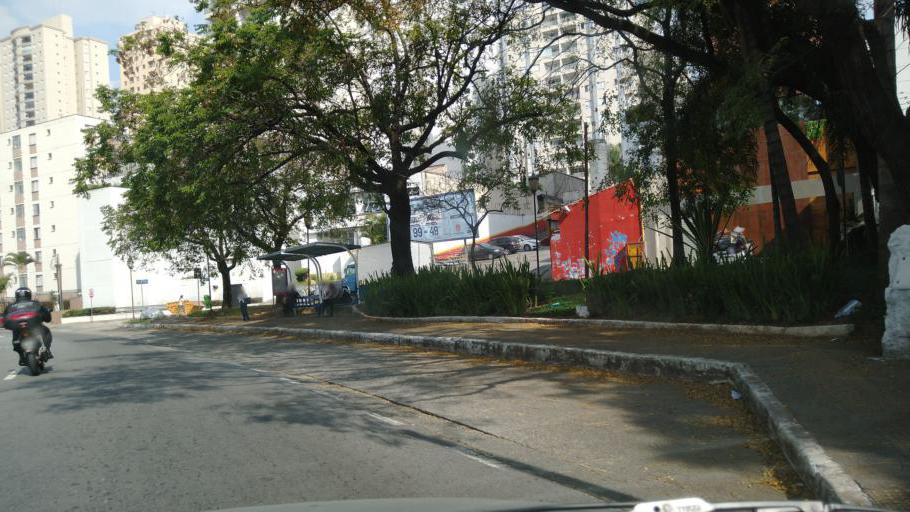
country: BR
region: Sao Paulo
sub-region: Guarulhos
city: Guarulhos
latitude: -23.4706
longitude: -46.5344
